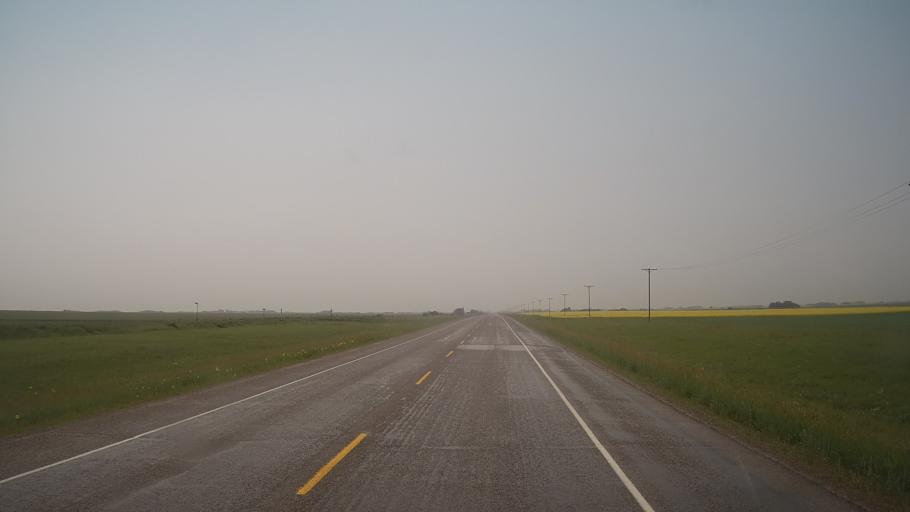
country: CA
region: Saskatchewan
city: Biggar
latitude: 52.1469
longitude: -108.2139
